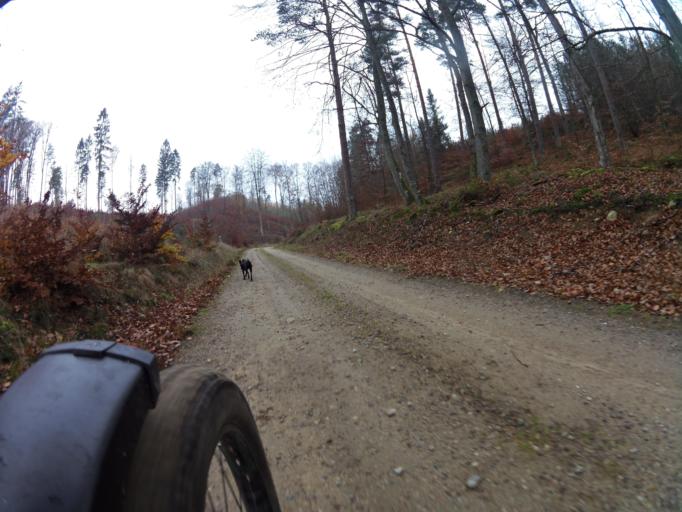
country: PL
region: Pomeranian Voivodeship
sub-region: Powiat pucki
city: Krokowa
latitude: 54.7118
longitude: 18.1434
